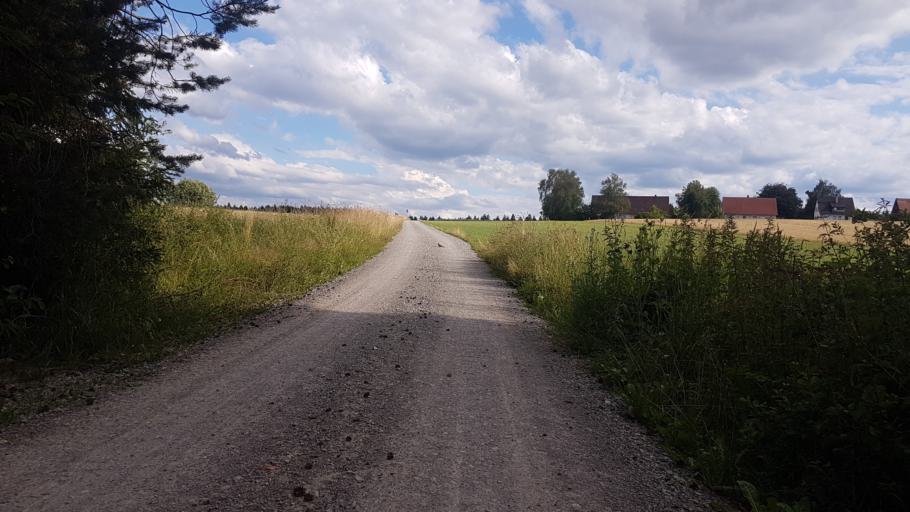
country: DE
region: Baden-Wuerttemberg
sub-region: Freiburg Region
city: Monchweiler
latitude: 48.0649
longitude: 8.4101
